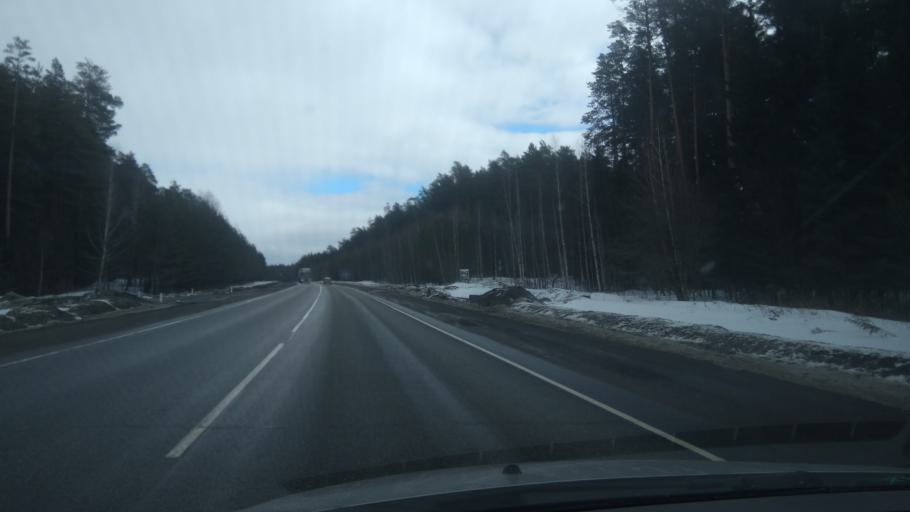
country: RU
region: Sverdlovsk
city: Achit
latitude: 56.7799
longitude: 57.9408
